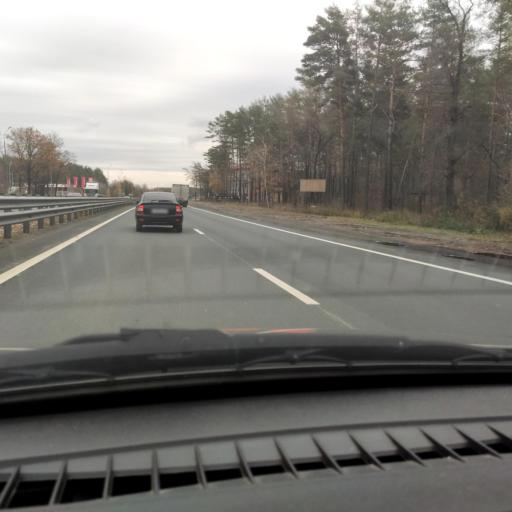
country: RU
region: Samara
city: Zhigulevsk
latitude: 53.5117
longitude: 49.5720
